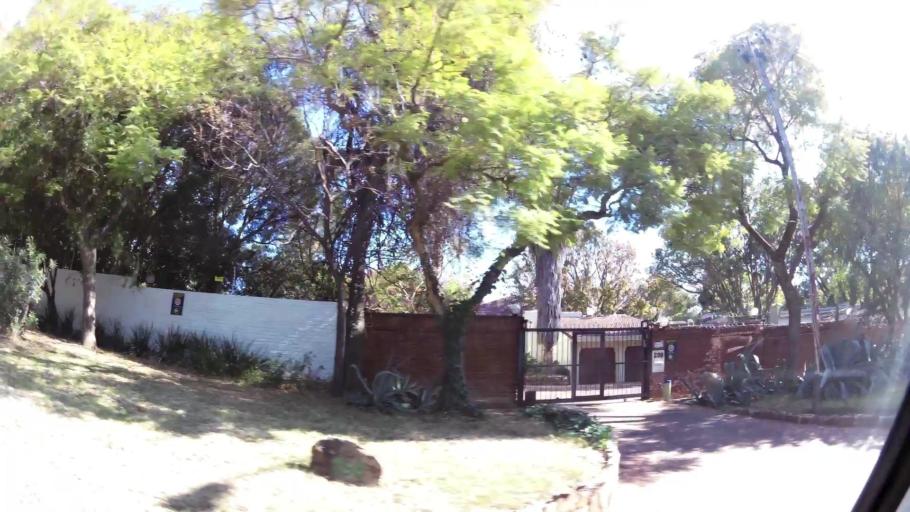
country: ZA
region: Gauteng
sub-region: City of Tshwane Metropolitan Municipality
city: Pretoria
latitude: -25.7924
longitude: 28.2405
